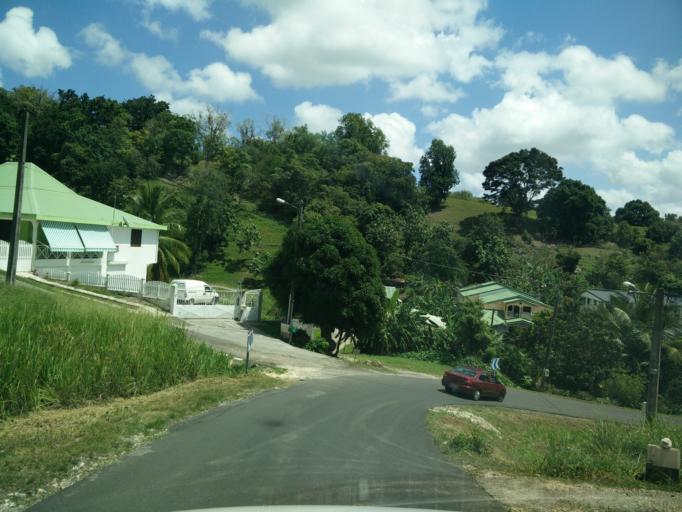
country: GP
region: Guadeloupe
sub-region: Guadeloupe
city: Les Abymes
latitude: 16.2691
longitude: -61.4907
